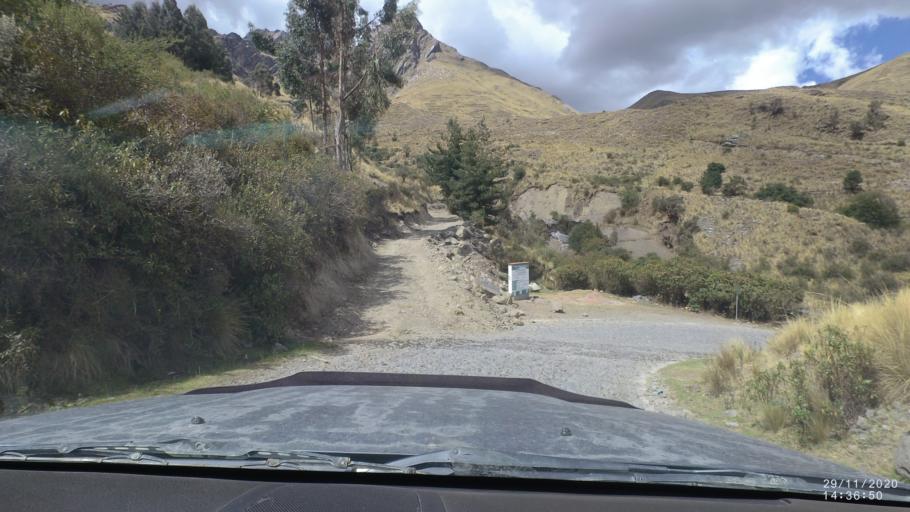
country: BO
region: Cochabamba
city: Sipe Sipe
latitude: -17.2683
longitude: -66.3287
